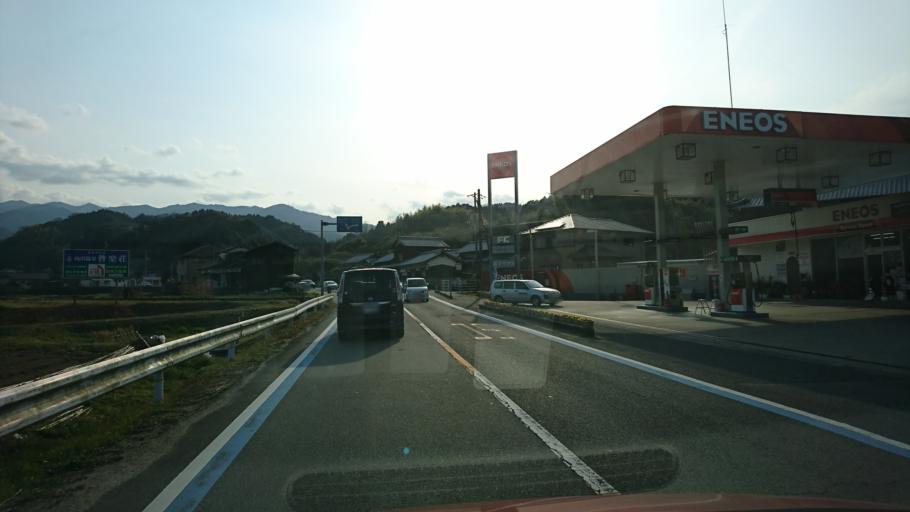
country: JP
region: Ehime
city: Hojo
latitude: 34.0040
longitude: 132.9384
